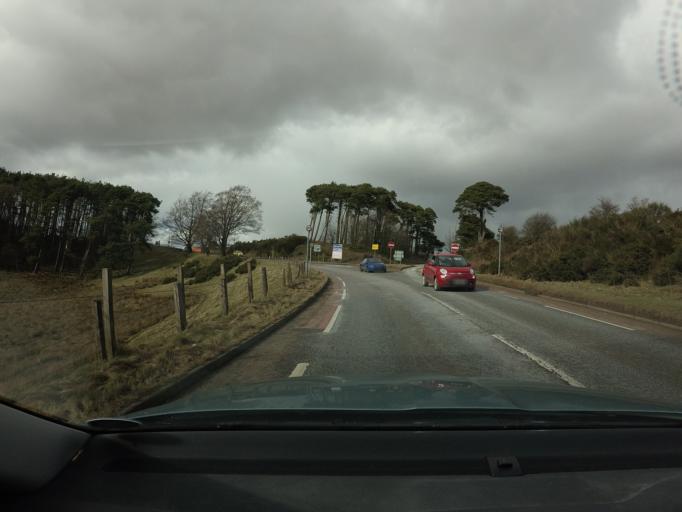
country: GB
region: Scotland
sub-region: South Lanarkshire
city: Lanark
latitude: 55.6587
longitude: -3.7278
